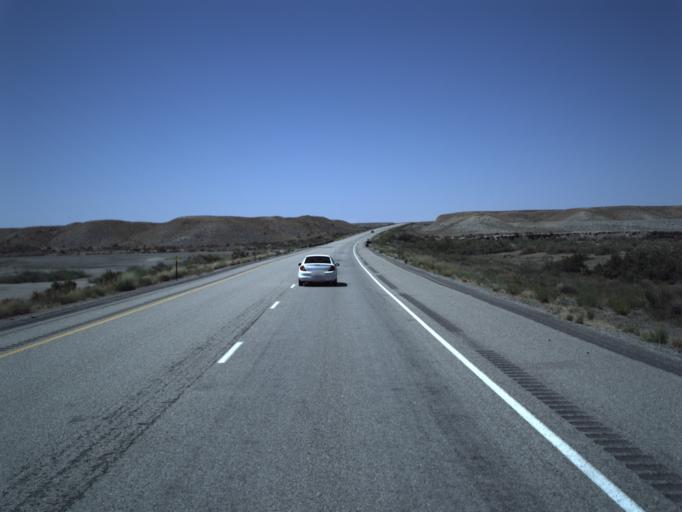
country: US
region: Utah
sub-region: Grand County
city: Moab
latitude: 38.9785
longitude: -109.3504
